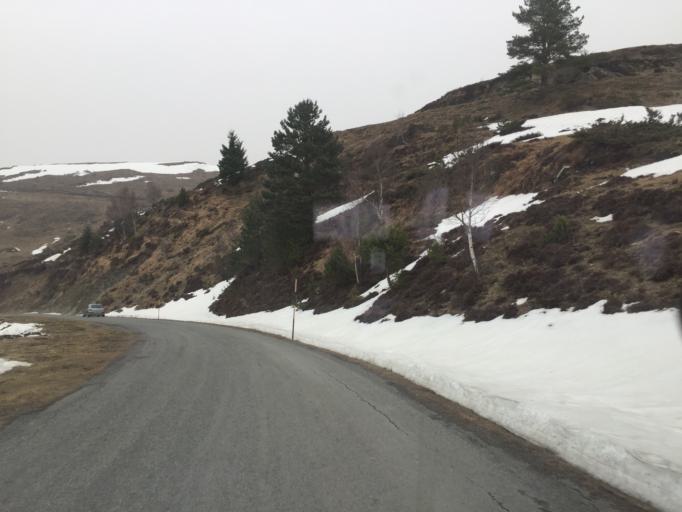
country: FR
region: Midi-Pyrenees
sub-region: Departement des Hautes-Pyrenees
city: Saint-Lary-Soulan
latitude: 42.7938
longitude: 0.3816
